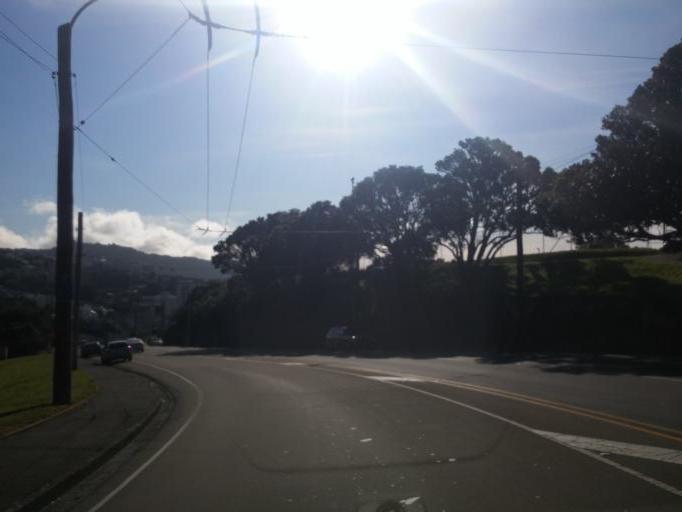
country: NZ
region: Wellington
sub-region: Wellington City
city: Wellington
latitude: -41.3025
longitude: 174.7697
